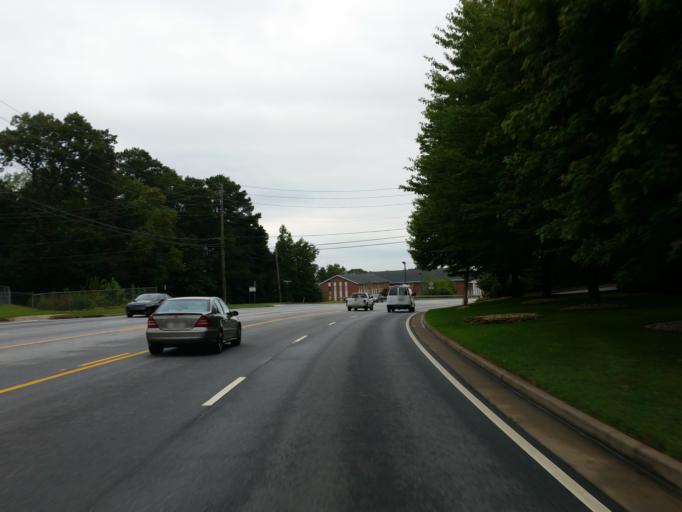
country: US
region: Georgia
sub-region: Cobb County
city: Mableton
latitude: 33.8134
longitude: -84.5413
